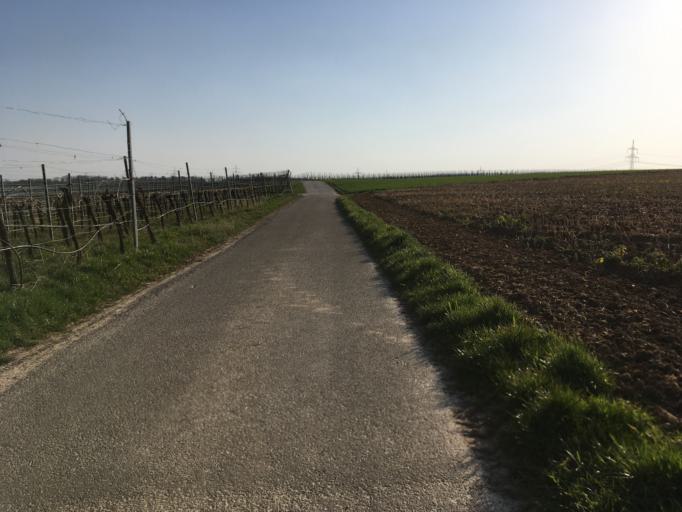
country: DE
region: Baden-Wuerttemberg
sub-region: Regierungsbezirk Stuttgart
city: Lauffen am Neckar
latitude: 49.0762
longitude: 9.1300
